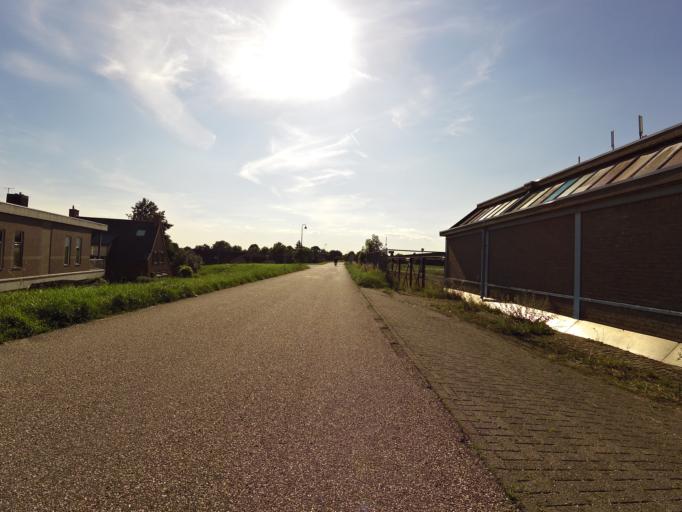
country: NL
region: Gelderland
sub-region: Gemeente Zevenaar
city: Zevenaar
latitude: 51.8671
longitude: 6.0485
